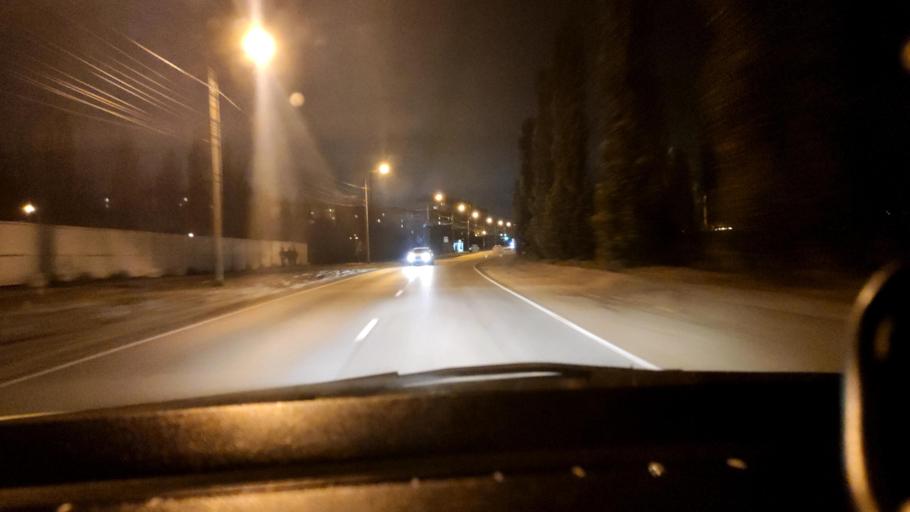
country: RU
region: Voronezj
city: Pridonskoy
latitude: 51.6221
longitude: 39.0686
